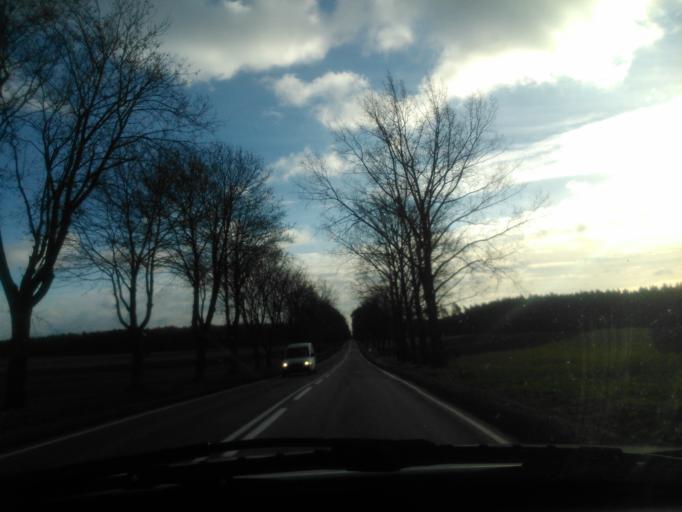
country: PL
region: Podlasie
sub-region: Powiat kolnenski
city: Maly Plock
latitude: 53.2971
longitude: 22.0382
